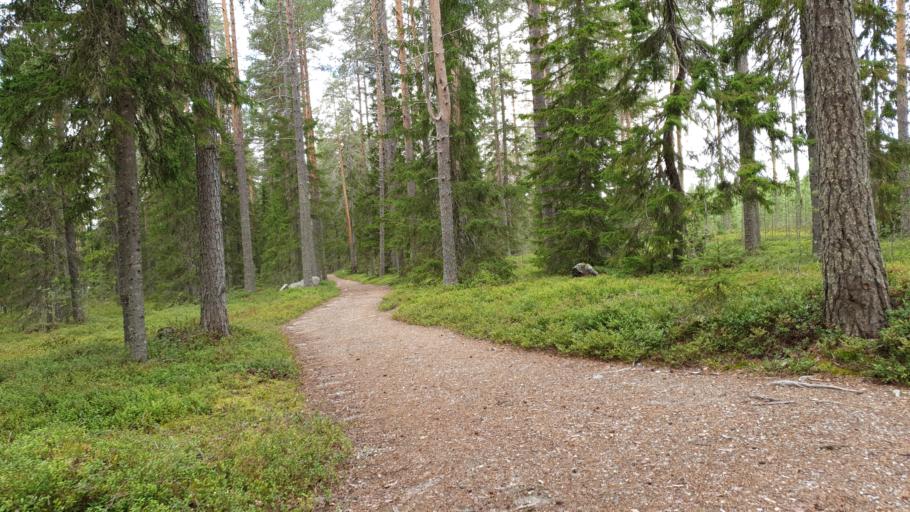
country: FI
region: Kainuu
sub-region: Kehys-Kainuu
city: Kuhmo
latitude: 64.3817
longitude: 29.8062
